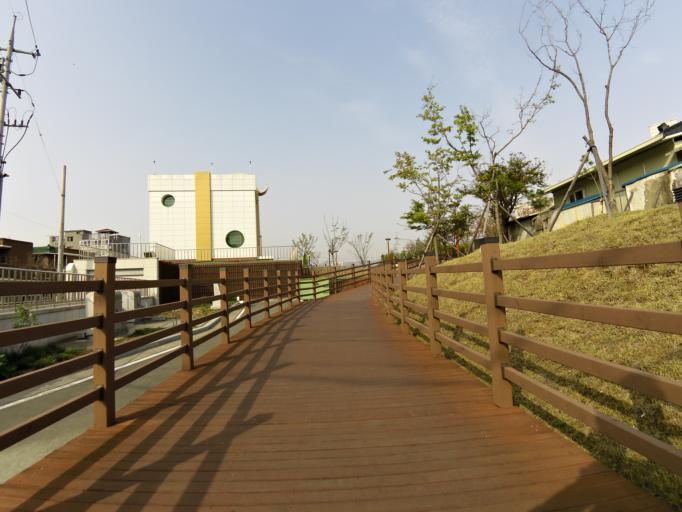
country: KR
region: Daegu
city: Daegu
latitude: 35.8883
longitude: 128.6368
